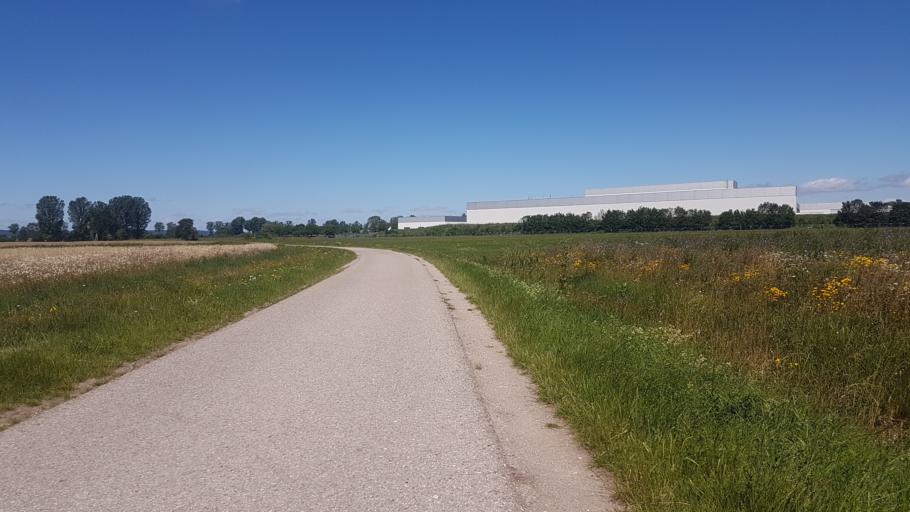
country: DE
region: Bavaria
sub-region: Regierungsbezirk Mittelfranken
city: Herrieden
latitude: 49.2255
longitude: 10.5111
